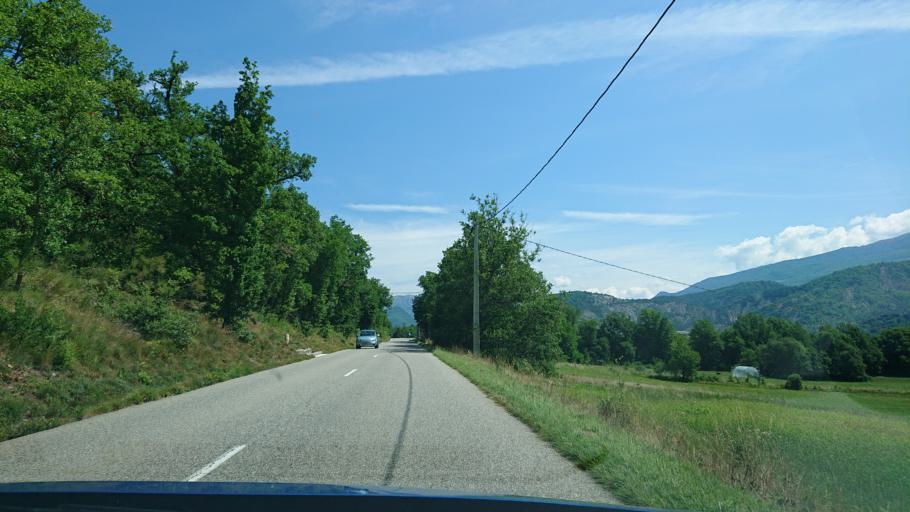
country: FR
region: Provence-Alpes-Cote d'Azur
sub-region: Departement des Alpes-de-Haute-Provence
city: Sisteron
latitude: 44.2783
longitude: 6.0113
